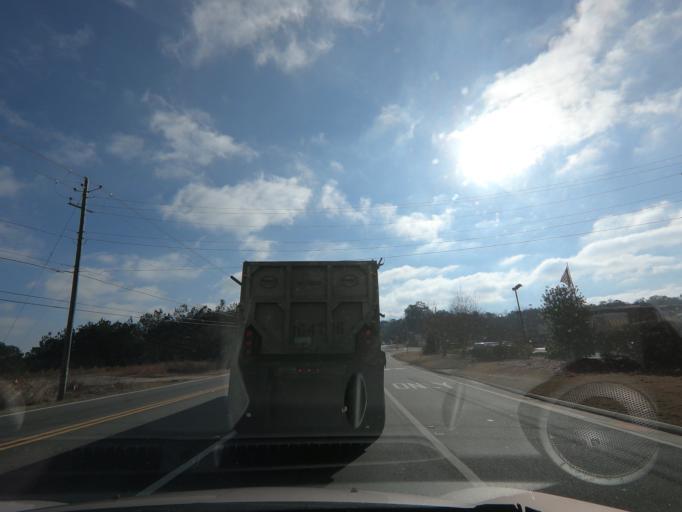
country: US
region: Georgia
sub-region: Cherokee County
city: Canton
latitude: 34.2365
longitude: -84.4527
